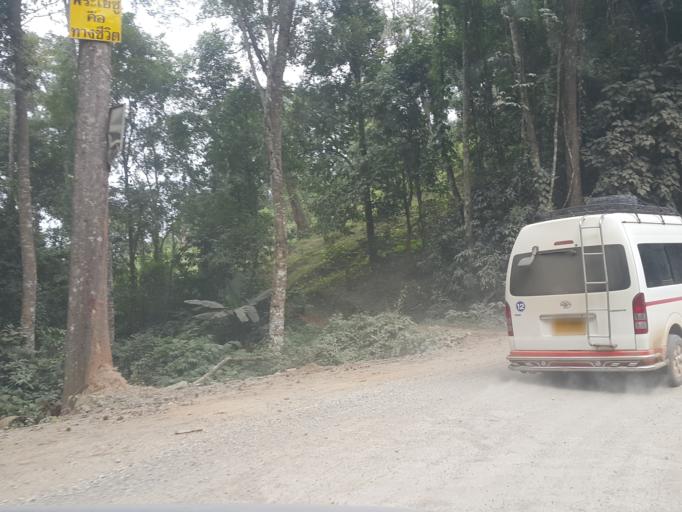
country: TH
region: Chiang Mai
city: Mae Taeng
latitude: 19.1357
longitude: 98.7028
